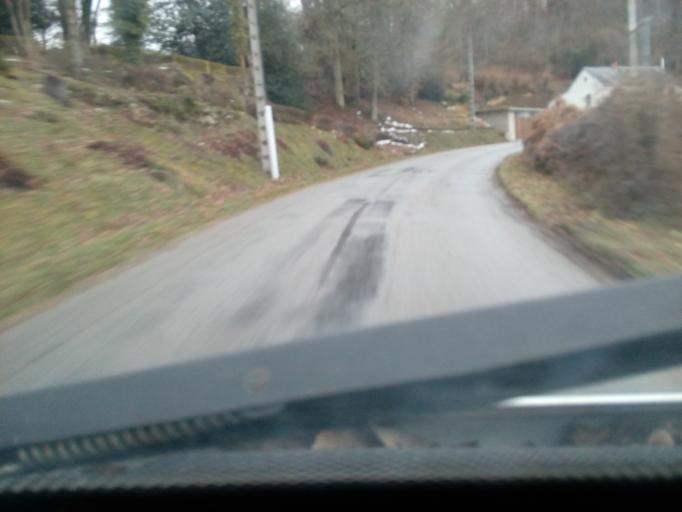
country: FR
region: Limousin
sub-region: Departement de la Creuse
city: Felletin
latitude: 45.8587
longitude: 2.2195
